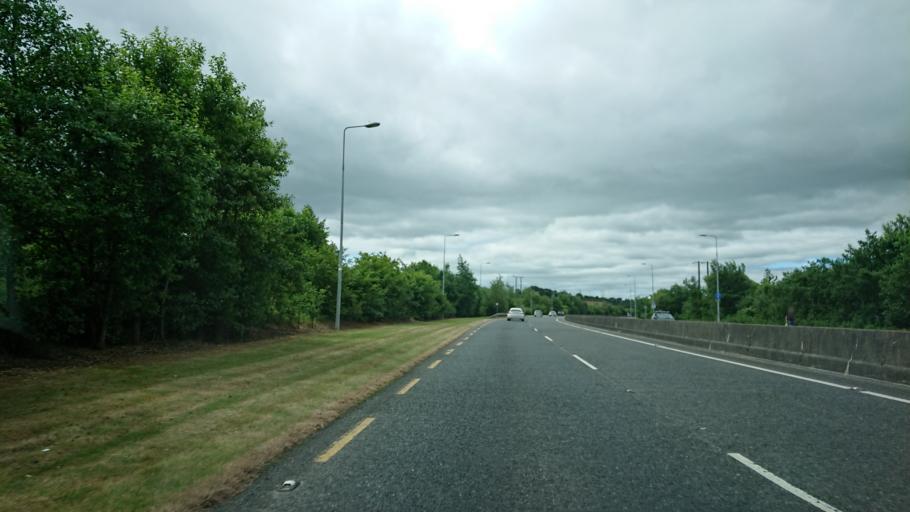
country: IE
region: Munster
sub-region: Waterford
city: Waterford
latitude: 52.2258
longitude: -7.1192
